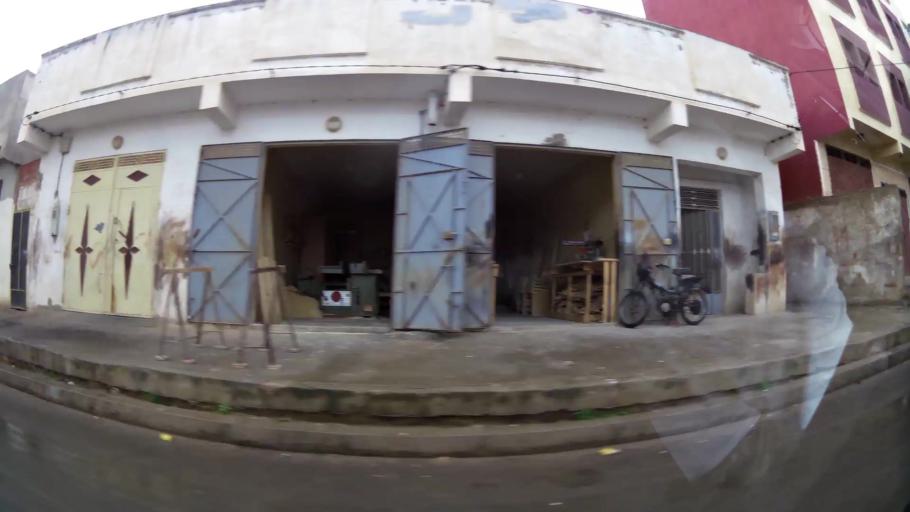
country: MA
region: Oriental
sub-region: Nador
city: Nador
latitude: 35.1495
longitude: -2.9905
